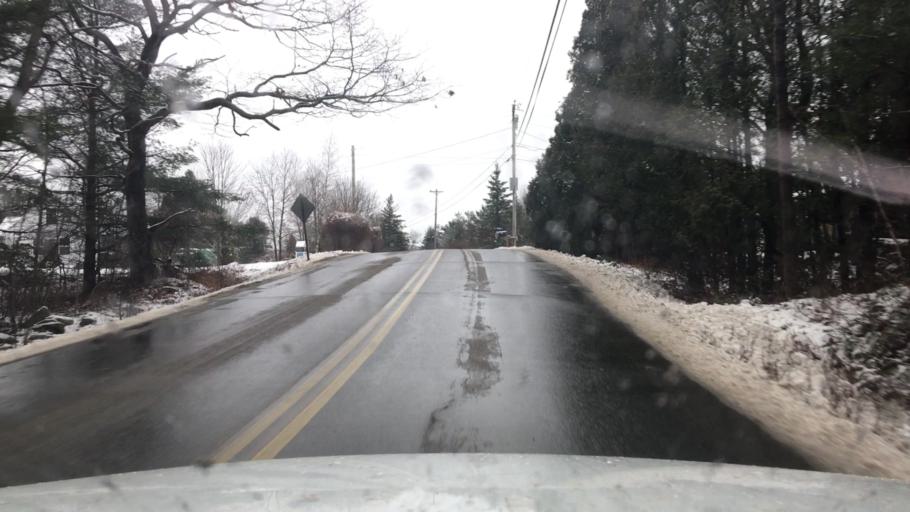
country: US
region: Maine
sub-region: Knox County
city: South Thomaston
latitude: 44.0844
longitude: -69.1387
